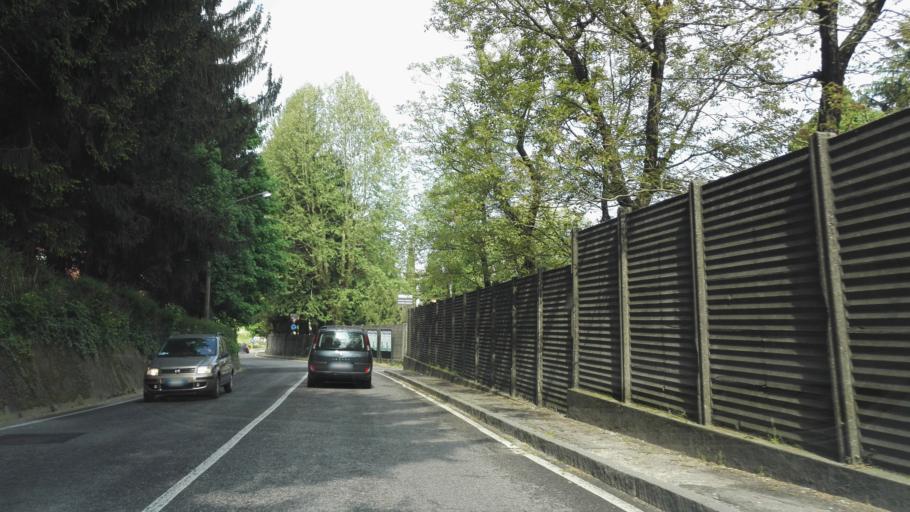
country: IT
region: Lombardy
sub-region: Provincia di Como
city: Como
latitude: 45.7995
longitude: 9.0984
